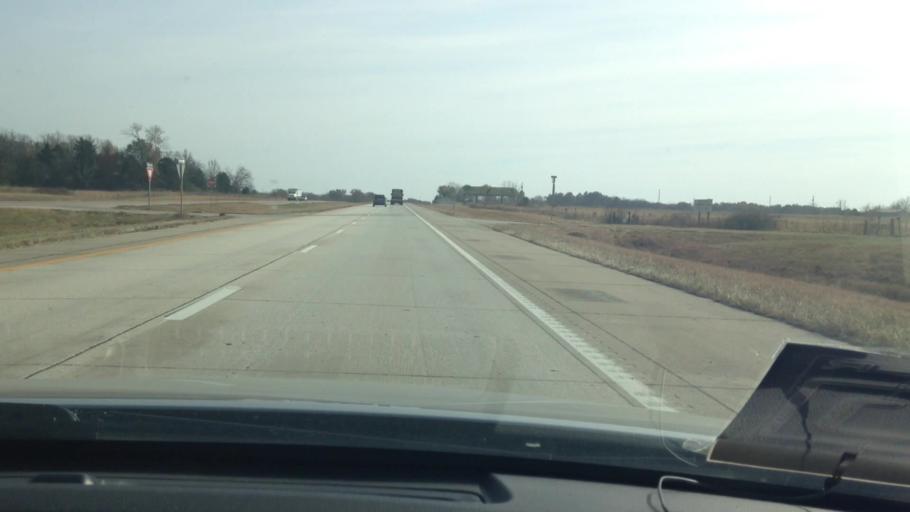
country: US
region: Missouri
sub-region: Henry County
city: Clinton
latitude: 38.4067
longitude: -93.8460
